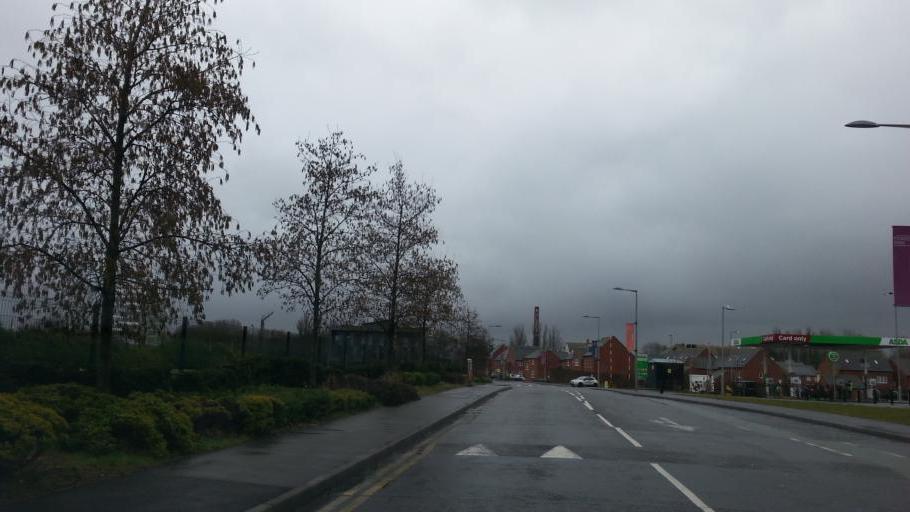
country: GB
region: England
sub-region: City of Leicester
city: Leicester
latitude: 52.6529
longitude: -1.1372
